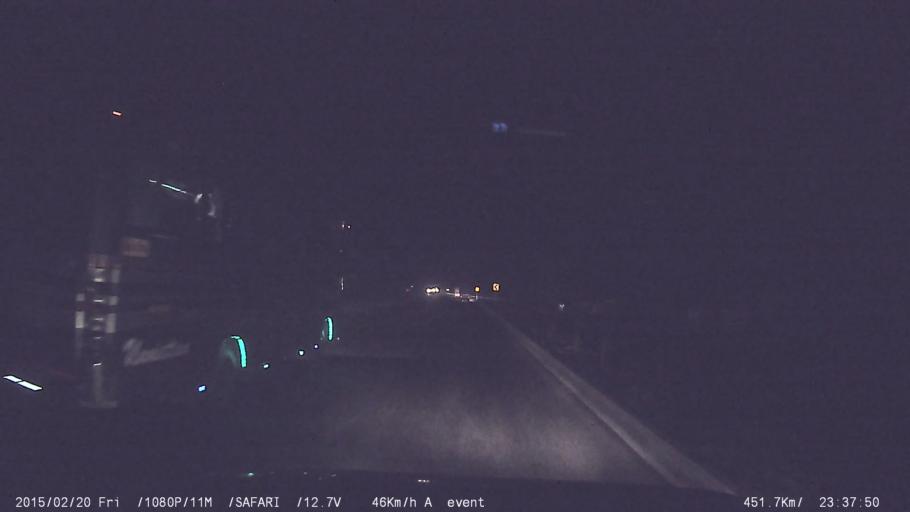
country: IN
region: Kerala
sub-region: Palakkad district
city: Palakkad
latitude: 10.7379
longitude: 76.6221
